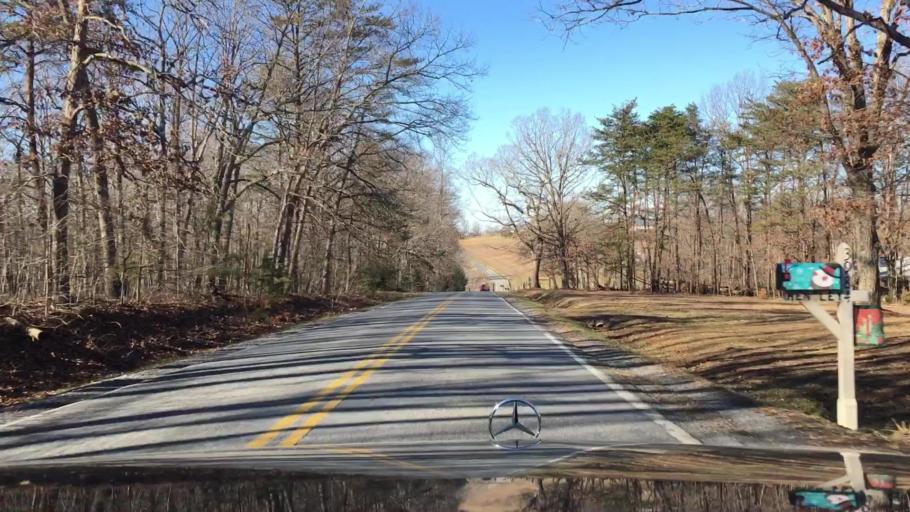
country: US
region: Virginia
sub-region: Pittsylvania County
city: Motley
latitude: 37.1853
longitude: -79.4179
